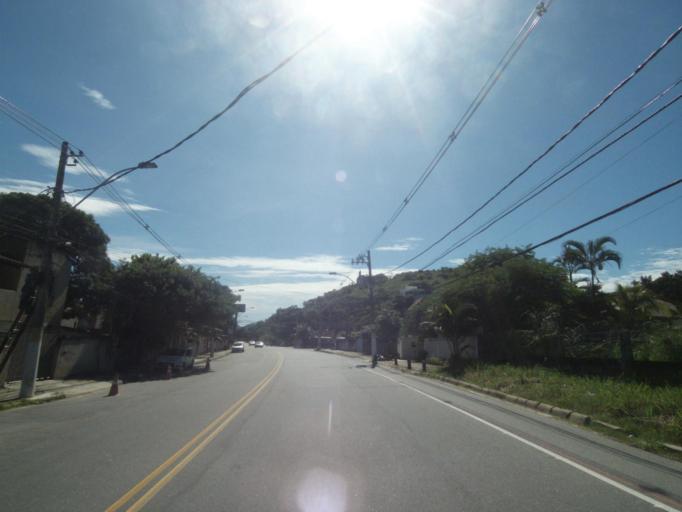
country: BR
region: Rio de Janeiro
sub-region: Niteroi
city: Niteroi
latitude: -22.9543
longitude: -43.0671
